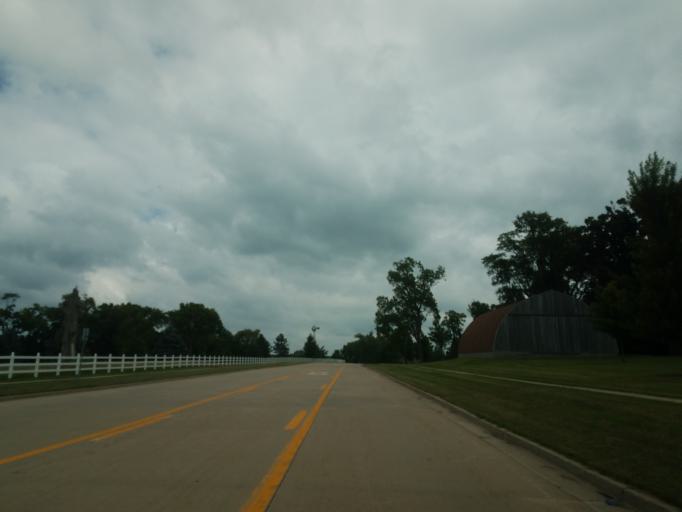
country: US
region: Illinois
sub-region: McLean County
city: Twin Grove
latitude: 40.4438
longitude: -89.0504
